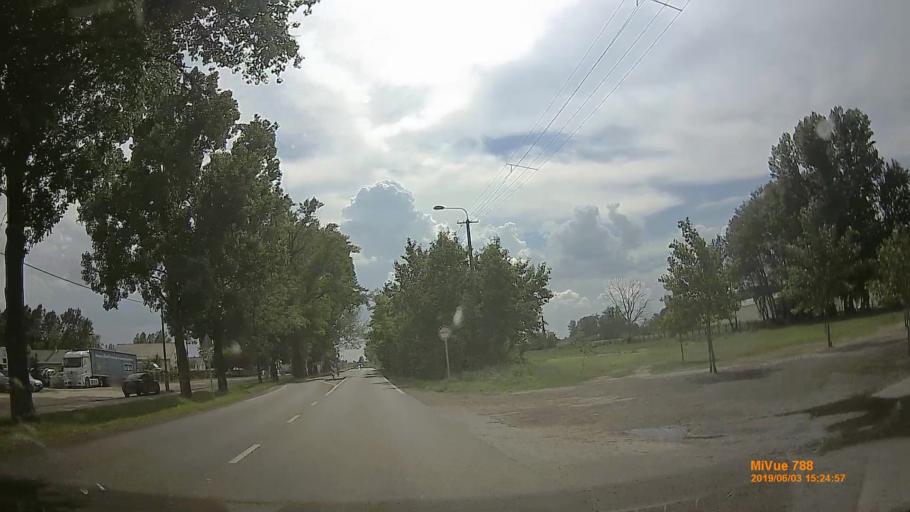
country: HU
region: Bacs-Kiskun
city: Tazlar
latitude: 46.6128
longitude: 19.4723
